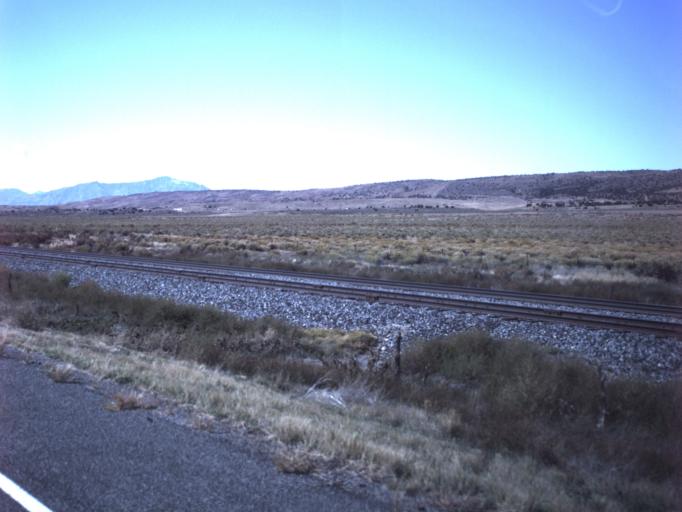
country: US
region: Utah
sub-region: Juab County
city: Nephi
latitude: 39.5162
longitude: -111.9432
